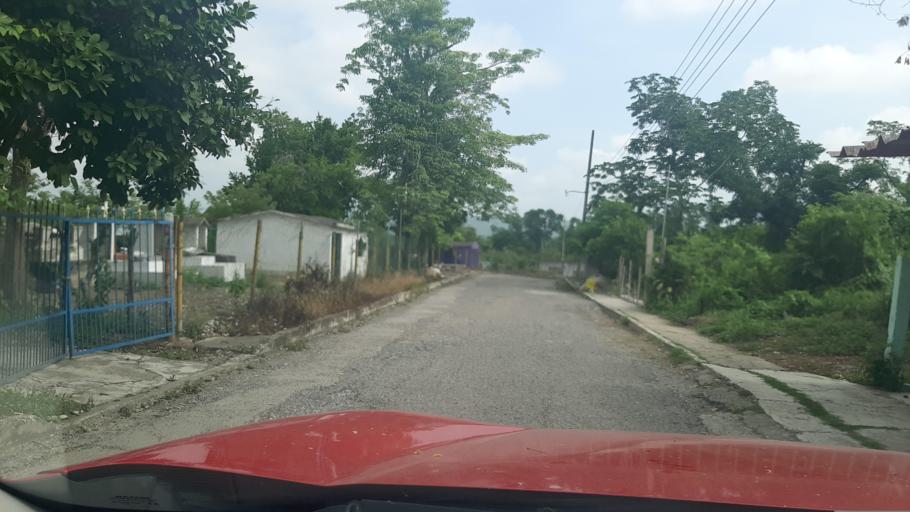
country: MX
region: Veracruz
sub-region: Coatzintla
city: Corralillos
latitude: 20.4844
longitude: -97.5034
